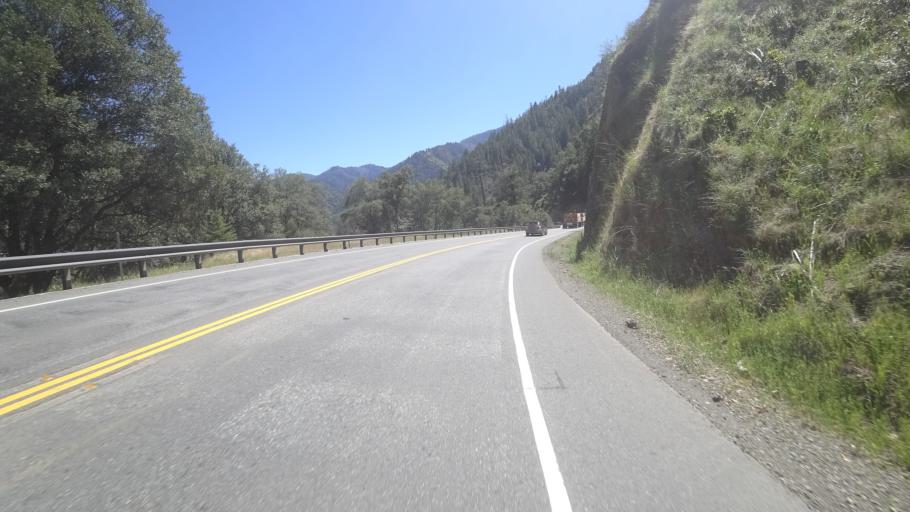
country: US
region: California
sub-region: Humboldt County
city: Willow Creek
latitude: 40.7970
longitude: -123.4611
